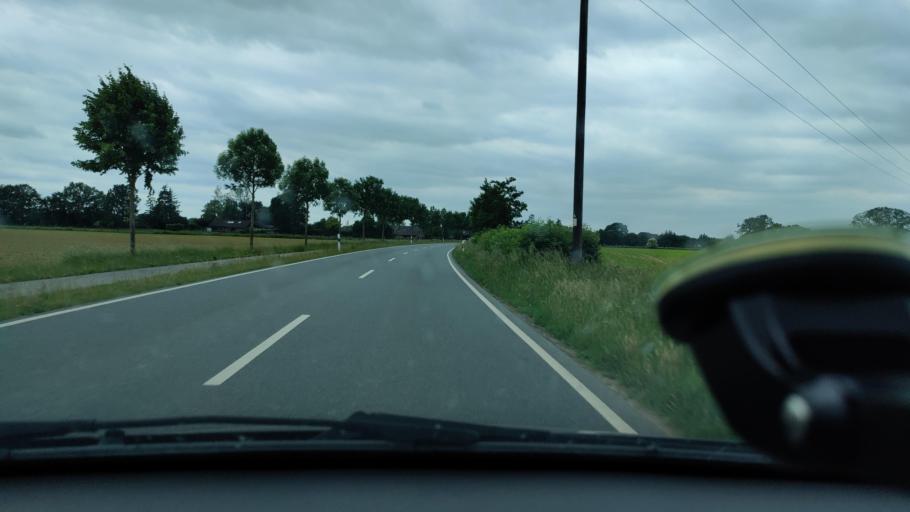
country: DE
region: North Rhine-Westphalia
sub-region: Regierungsbezirk Dusseldorf
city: Goch
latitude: 51.6963
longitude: 6.0891
